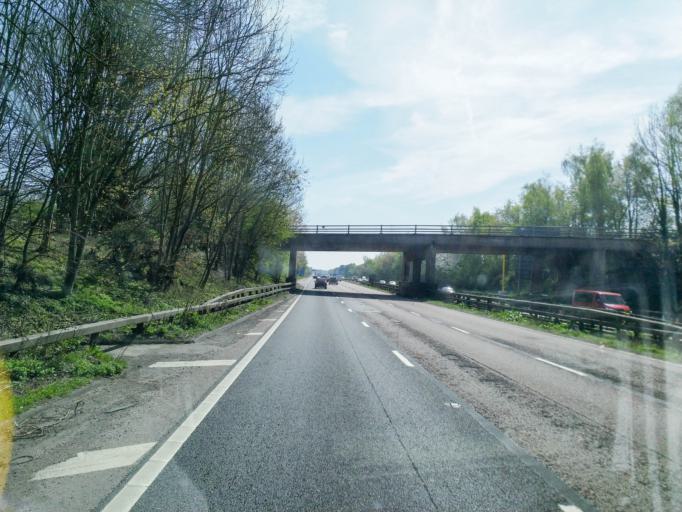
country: GB
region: England
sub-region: Kent
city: Ashford
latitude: 51.1569
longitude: 0.8771
